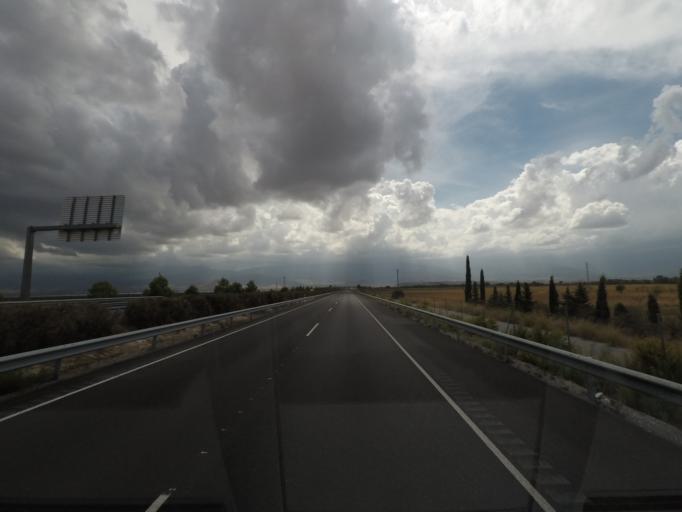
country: ES
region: Andalusia
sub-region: Provincia de Granada
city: Albunan
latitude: 37.2530
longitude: -3.0816
